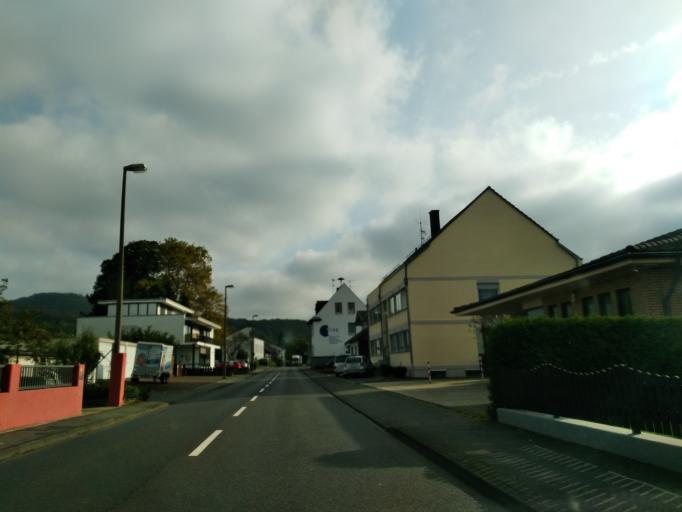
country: DE
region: North Rhine-Westphalia
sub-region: Regierungsbezirk Koln
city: Konigswinter
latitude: 50.6998
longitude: 7.1848
